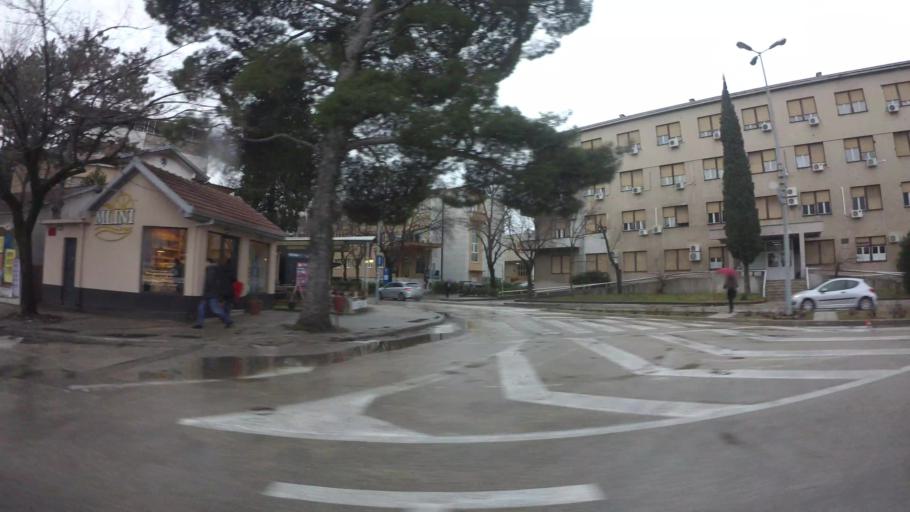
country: BA
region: Federation of Bosnia and Herzegovina
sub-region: Hercegovacko-Bosanski Kanton
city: Mostar
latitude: 43.3467
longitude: 17.8047
